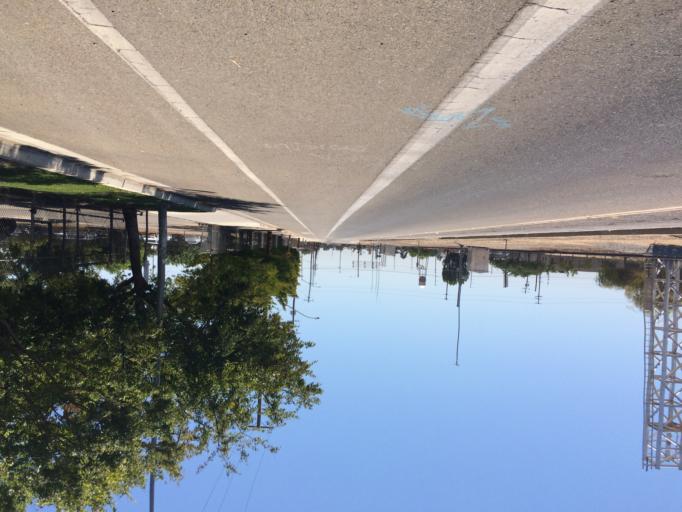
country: US
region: California
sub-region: Fresno County
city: Fresno
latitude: 36.7231
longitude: -119.7727
